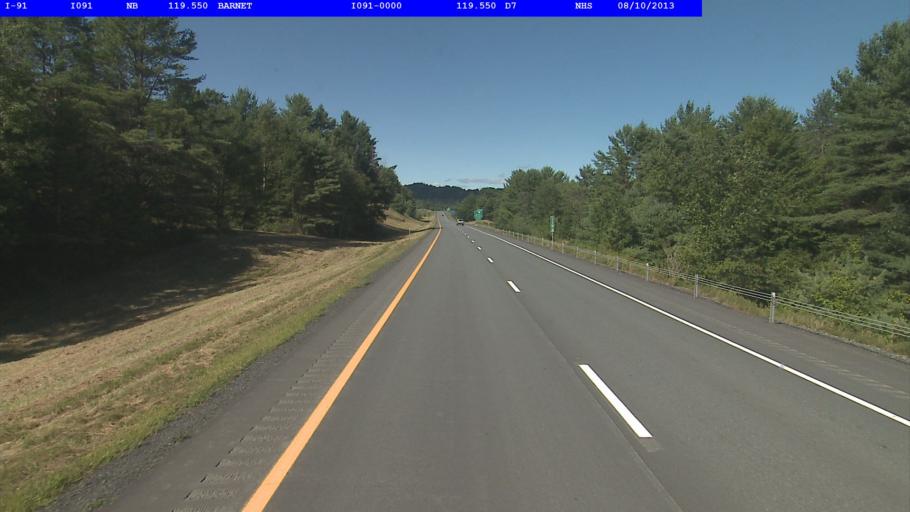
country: US
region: New Hampshire
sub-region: Grafton County
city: Woodsville
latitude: 44.2868
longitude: -72.0646
